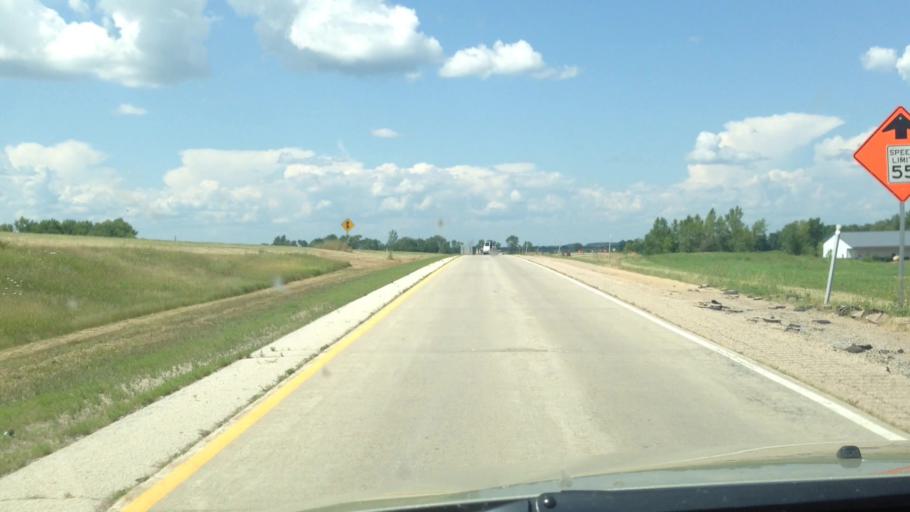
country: US
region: Wisconsin
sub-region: Brown County
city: Pulaski
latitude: 44.6751
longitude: -88.3086
